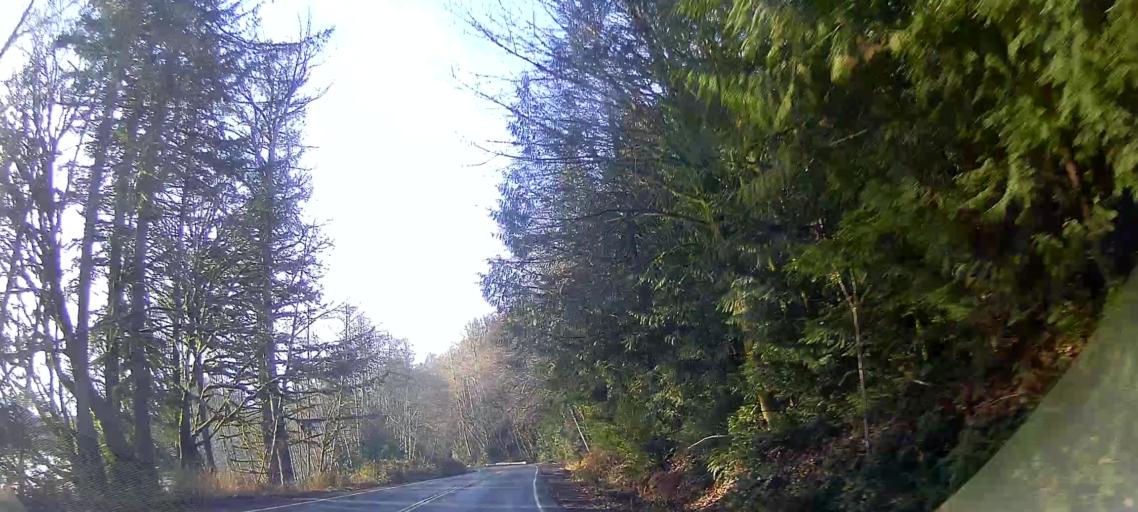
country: US
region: Washington
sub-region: Snohomish County
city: Darrington
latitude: 48.5672
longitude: -121.7994
